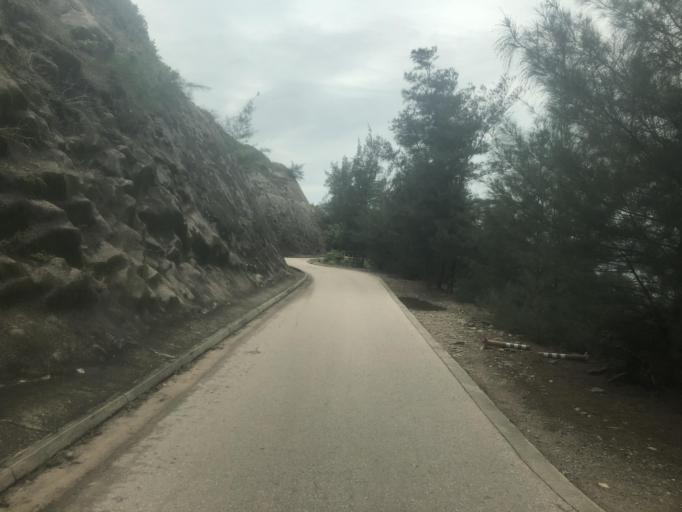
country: HK
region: Sai Kung
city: Sai Kung
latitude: 22.3605
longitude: 114.3701
